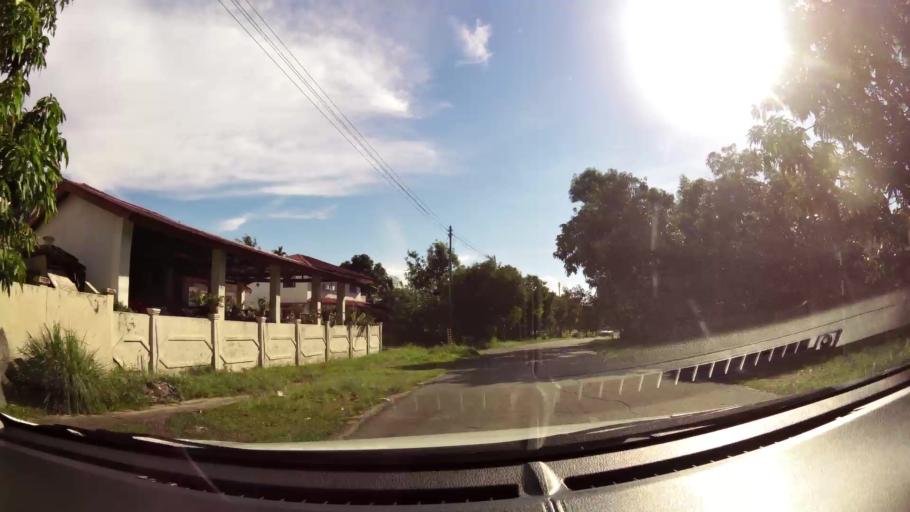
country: BN
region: Brunei and Muara
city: Bandar Seri Begawan
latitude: 4.9639
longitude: 114.9557
